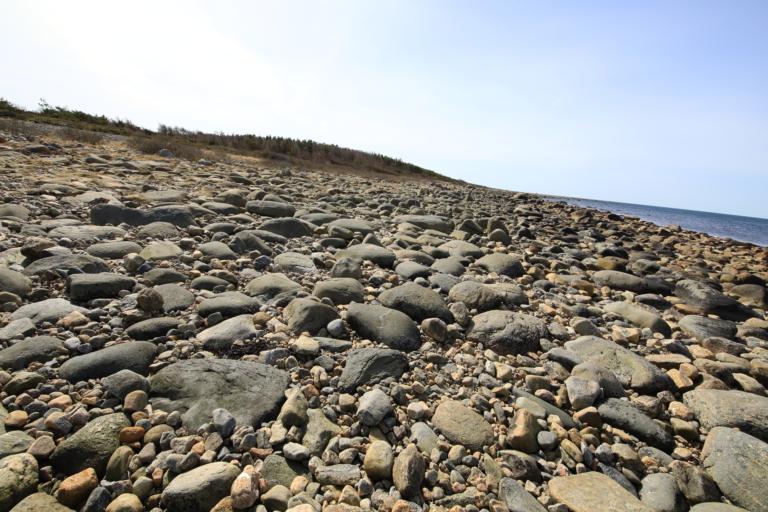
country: SE
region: Halland
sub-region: Kungsbacka Kommun
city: Frillesas
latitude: 57.2767
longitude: 12.1214
